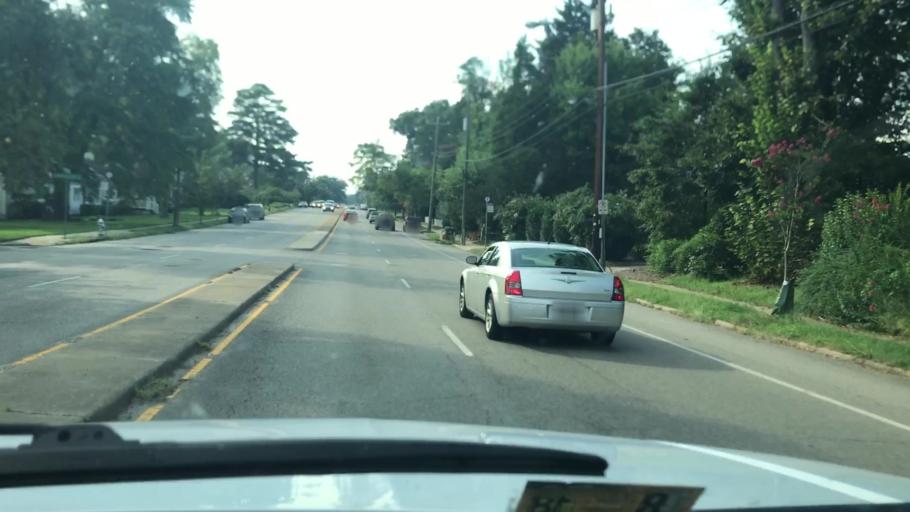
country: US
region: Virginia
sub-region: Henrico County
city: Tuckahoe
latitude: 37.5858
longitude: -77.5238
